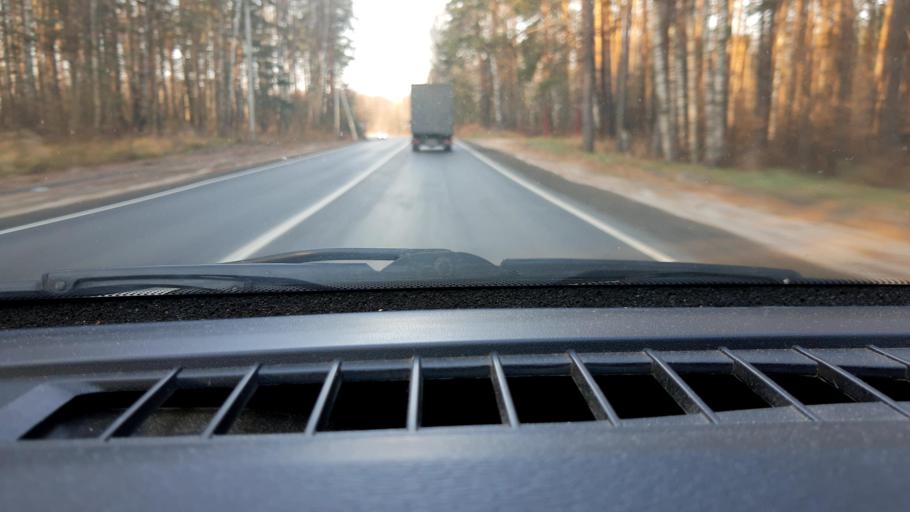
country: RU
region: Nizjnij Novgorod
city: Gorodets
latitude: 56.6139
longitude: 43.5872
